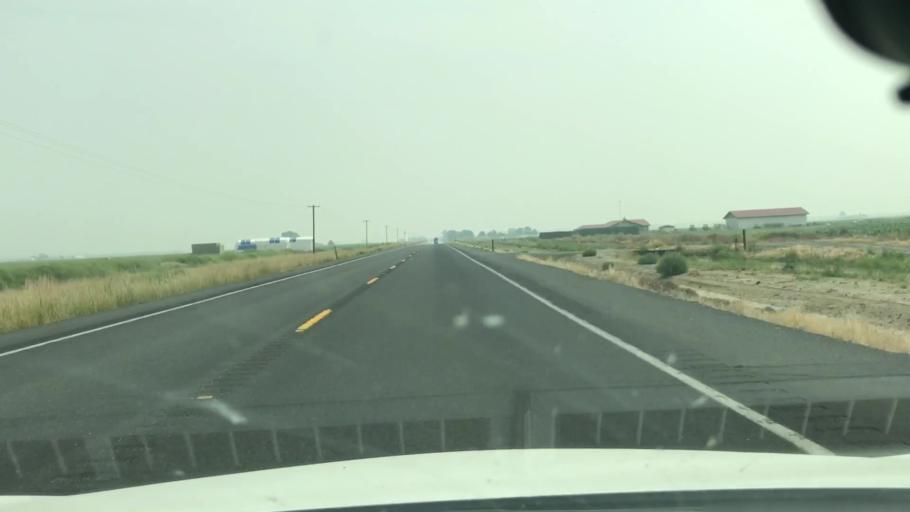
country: US
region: Washington
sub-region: Grant County
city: Quincy
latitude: 47.2341
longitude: -119.7931
